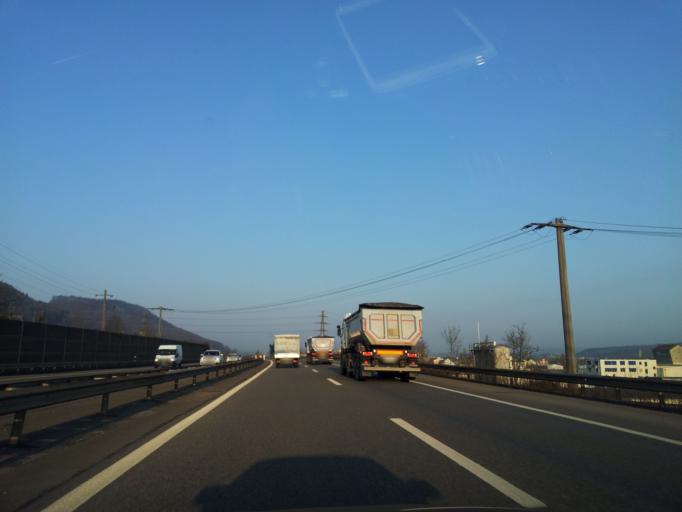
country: CH
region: Aargau
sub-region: Bezirk Rheinfelden
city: Stein
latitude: 47.5411
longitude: 7.9666
